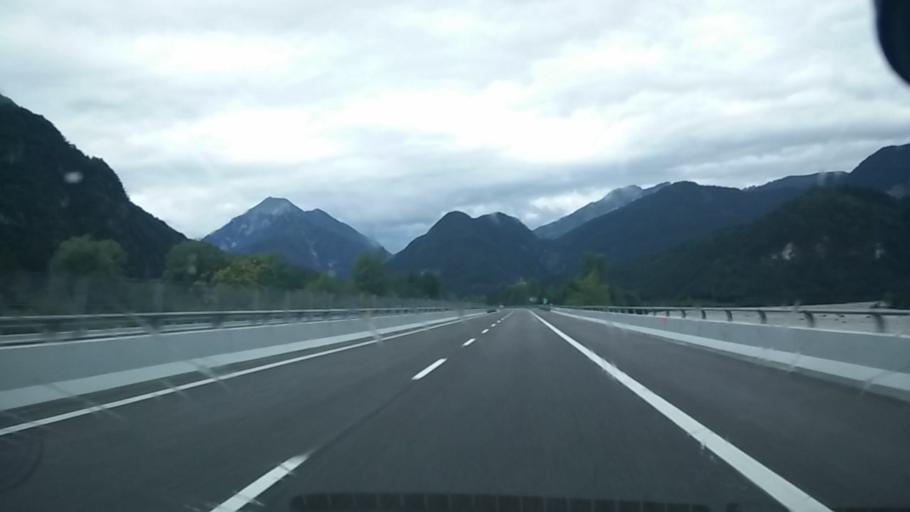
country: IT
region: Friuli Venezia Giulia
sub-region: Provincia di Udine
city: Resiutta
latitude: 46.3958
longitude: 13.2192
